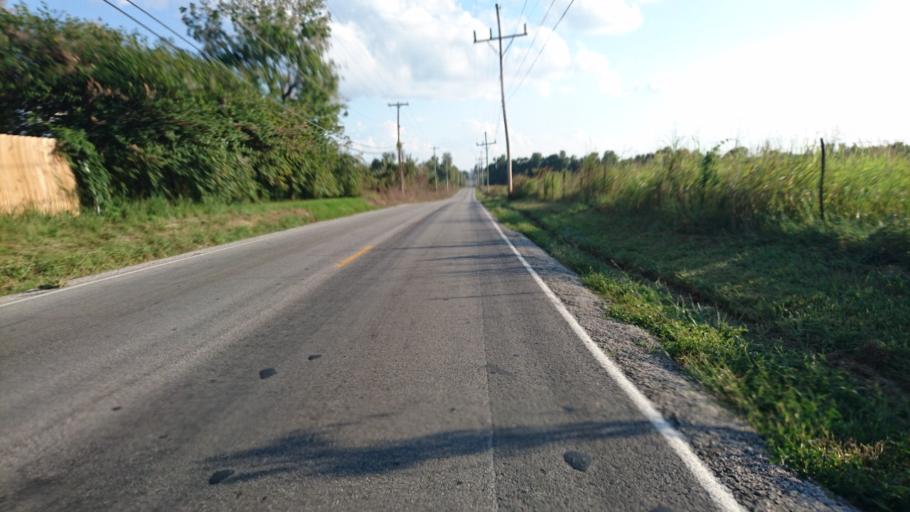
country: US
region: Missouri
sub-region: Greene County
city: Springfield
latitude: 37.2052
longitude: -93.3862
